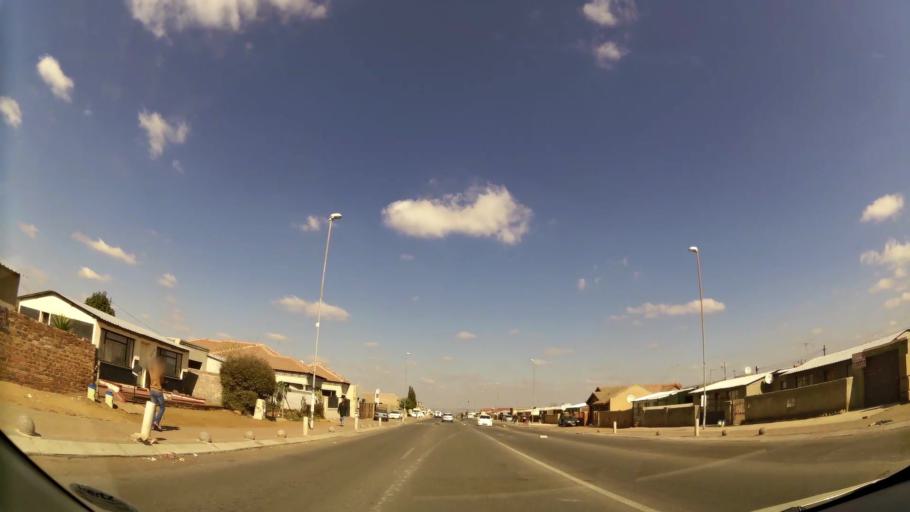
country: ZA
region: Gauteng
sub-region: West Rand District Municipality
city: Krugersdorp
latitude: -26.1596
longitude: 27.7824
